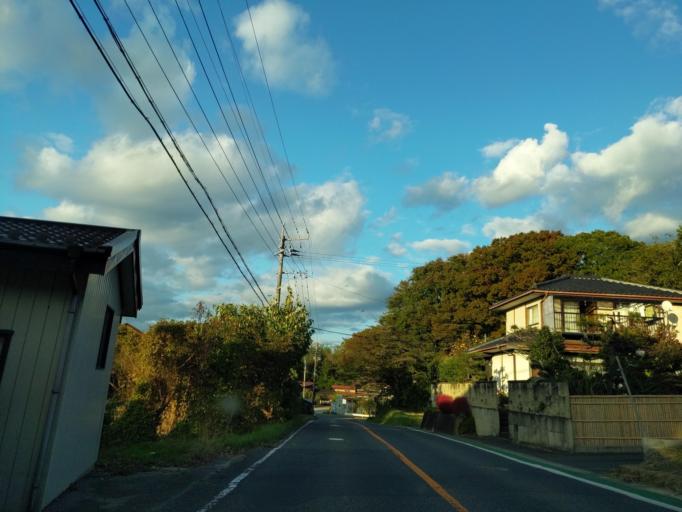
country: JP
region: Fukushima
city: Koriyama
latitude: 37.4317
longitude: 140.4209
